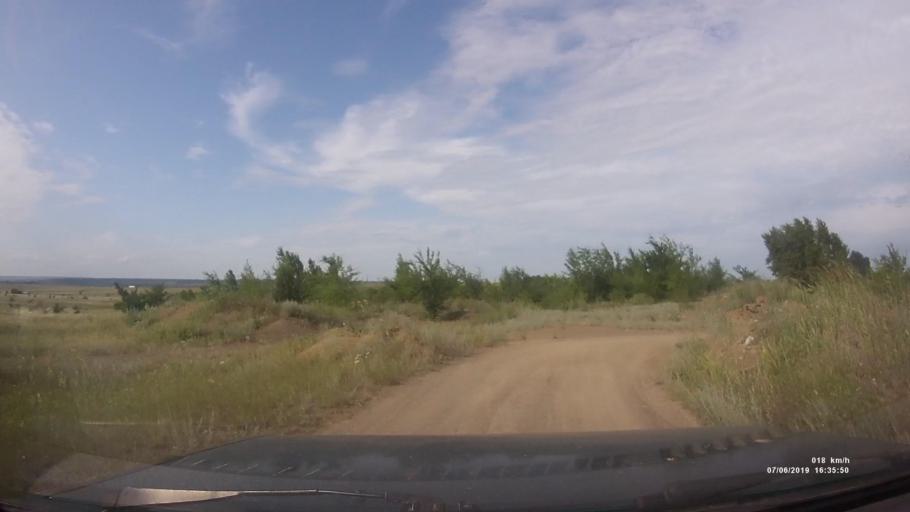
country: RU
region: Rostov
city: Staraya Stanitsa
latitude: 48.2524
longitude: 40.3494
